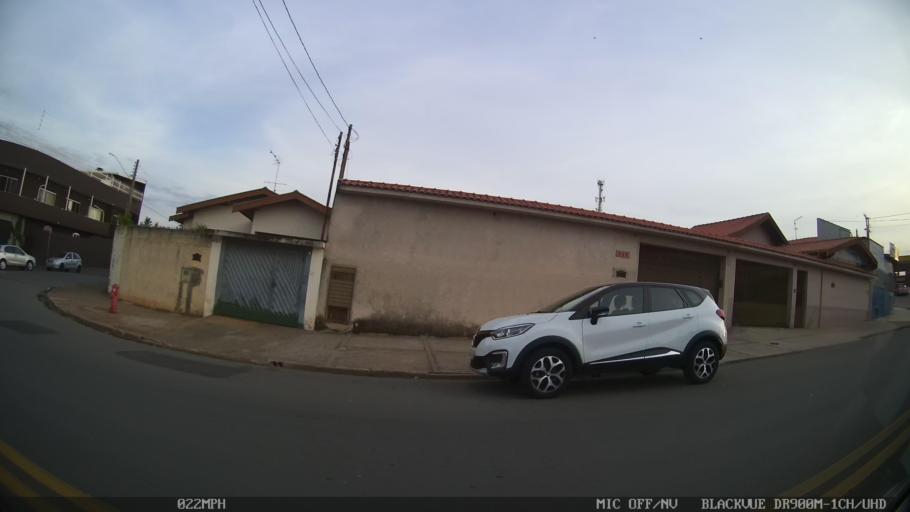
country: BR
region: Sao Paulo
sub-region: Limeira
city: Limeira
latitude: -22.5818
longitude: -47.4148
